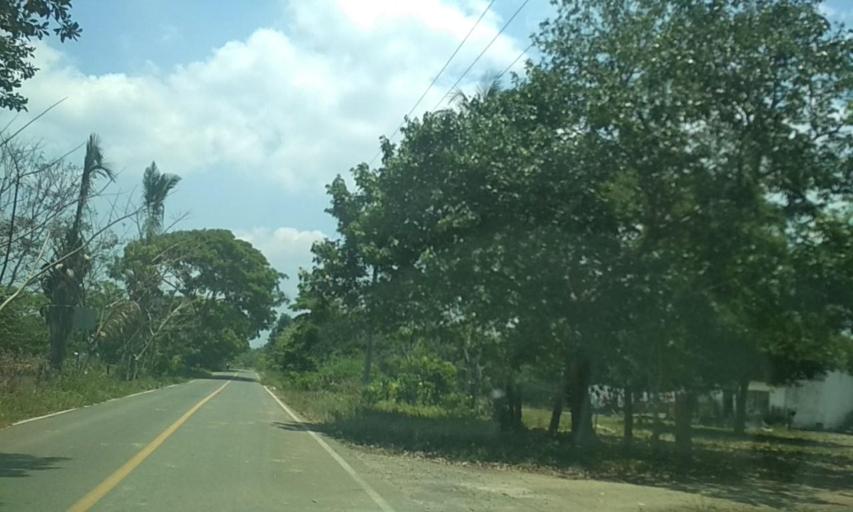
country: MX
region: Tabasco
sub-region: Huimanguillo
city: Francisco Rueda
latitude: 17.7499
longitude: -94.0432
